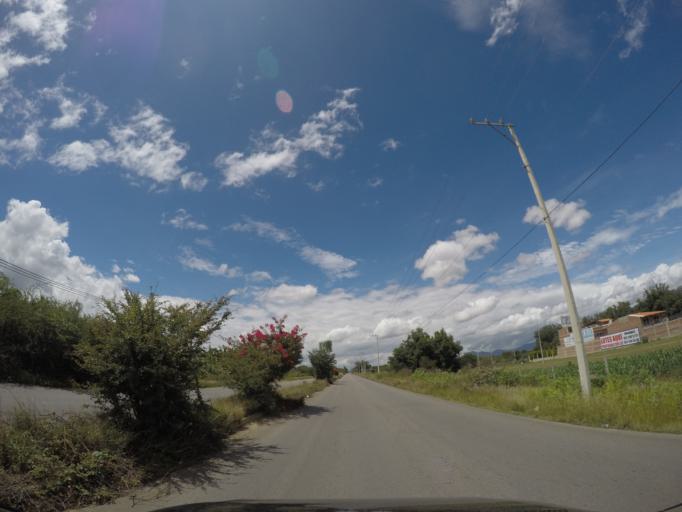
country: MX
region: Oaxaca
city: San Raymundo Jalpam
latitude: 16.9788
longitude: -96.7492
